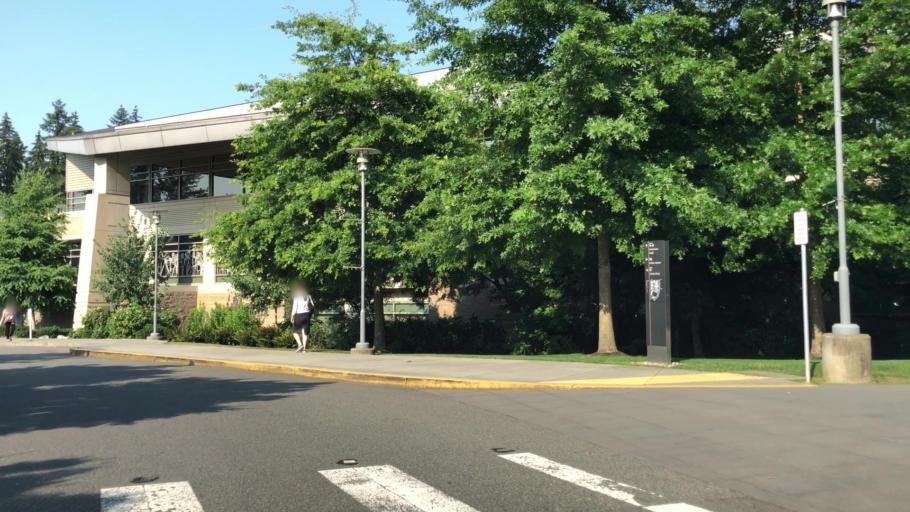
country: US
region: Washington
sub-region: King County
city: Redmond
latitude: 47.6426
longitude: -122.1361
